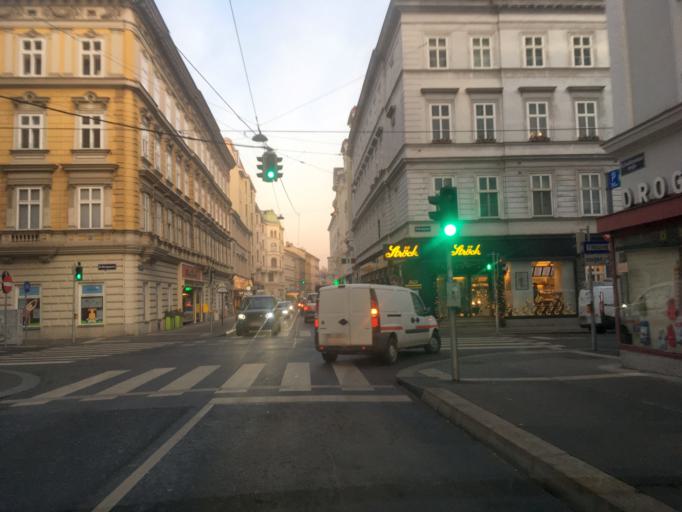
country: AT
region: Vienna
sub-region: Wien Stadt
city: Vienna
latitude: 48.2179
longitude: 16.3619
